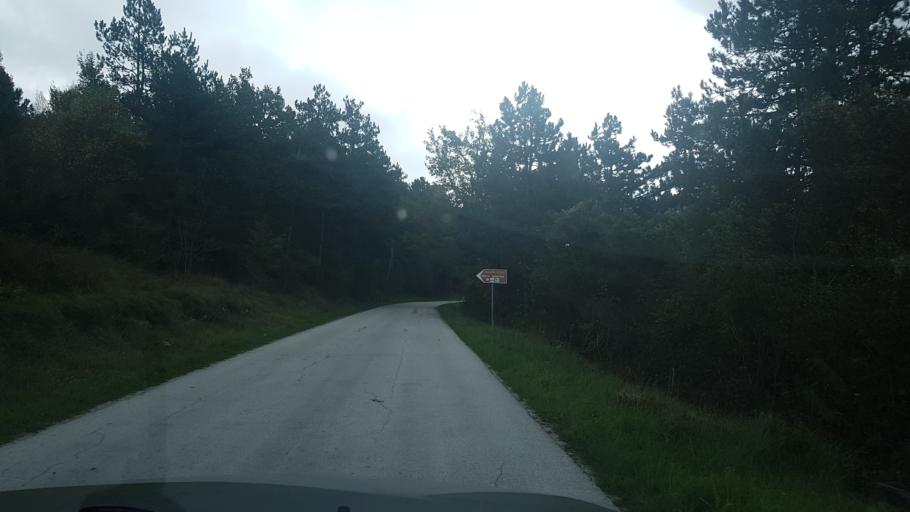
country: HR
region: Istarska
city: Buzet
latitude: 45.5014
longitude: 13.9939
